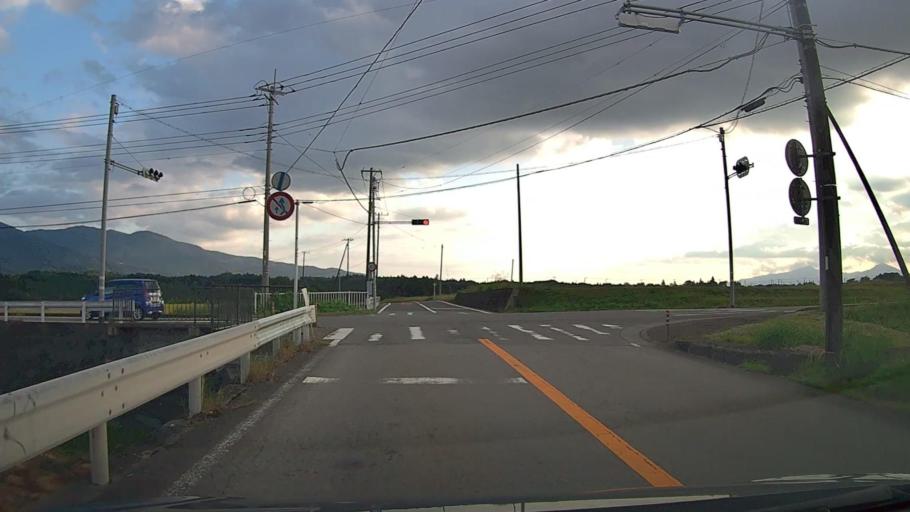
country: JP
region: Shizuoka
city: Gotemba
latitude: 35.3348
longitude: 138.9619
